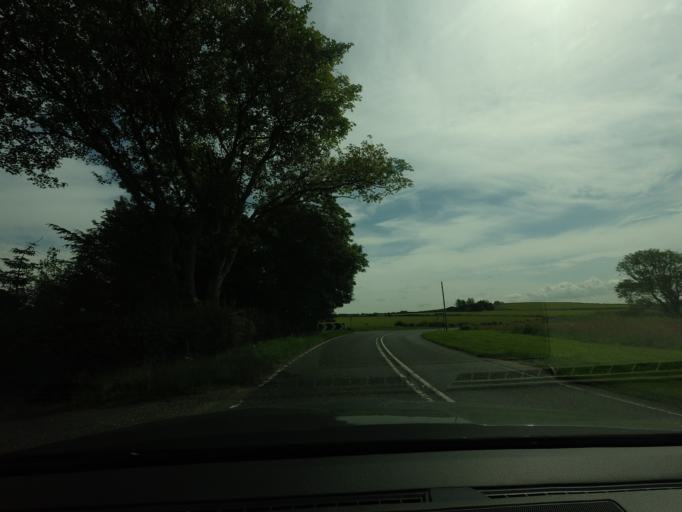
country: GB
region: Scotland
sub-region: Aberdeenshire
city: Rosehearty
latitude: 57.5783
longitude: -2.1755
